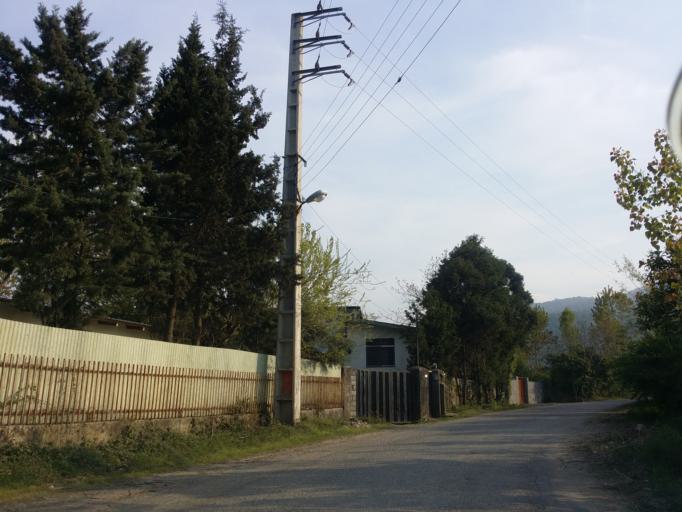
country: IR
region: Mazandaran
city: Chalus
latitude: 36.6651
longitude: 51.3657
